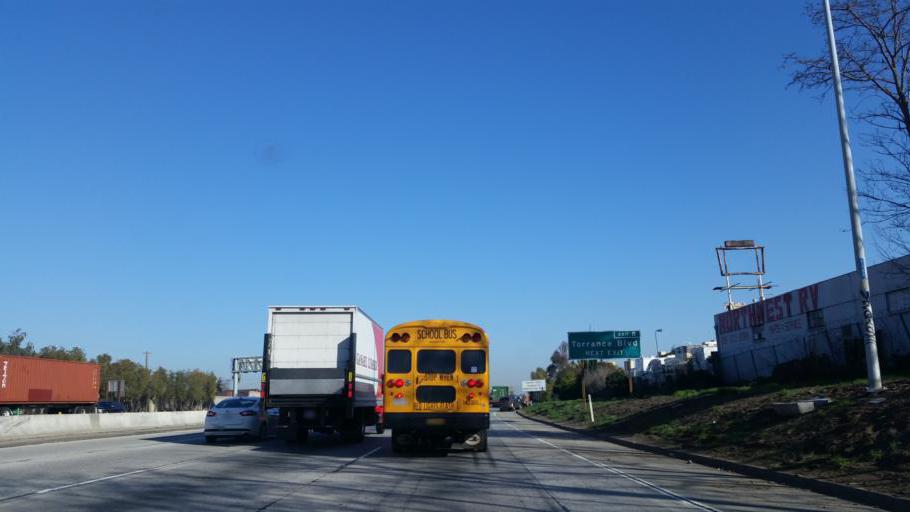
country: US
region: California
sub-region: Los Angeles County
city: Carson
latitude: 33.8365
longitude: -118.2871
